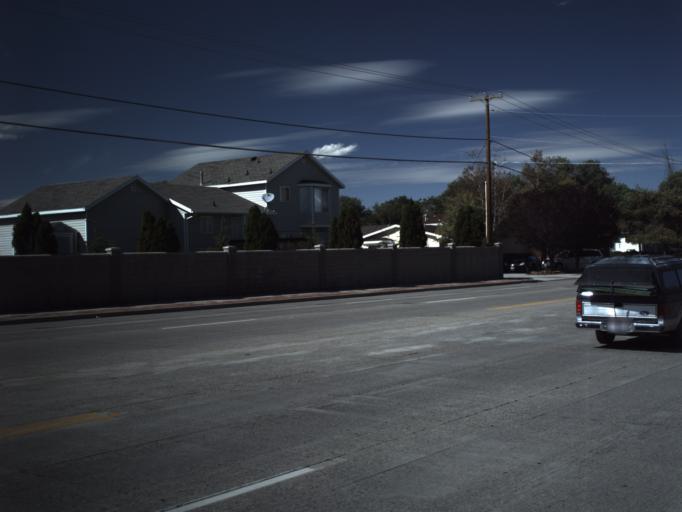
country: US
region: Utah
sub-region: Salt Lake County
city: West Jordan
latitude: 40.5993
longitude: -111.9386
